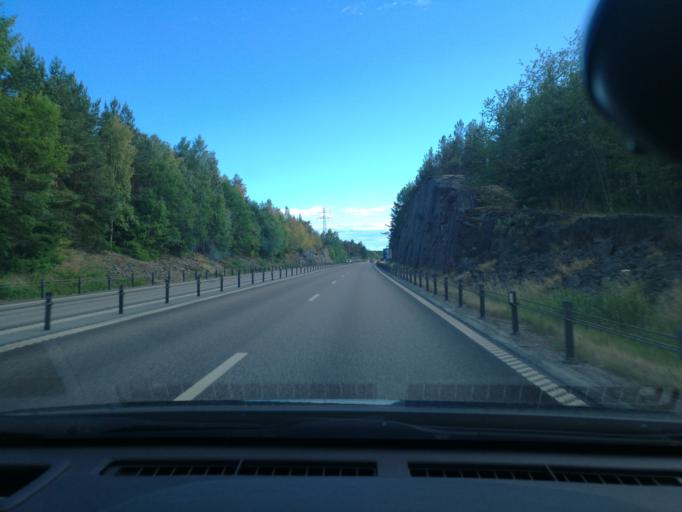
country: SE
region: Kalmar
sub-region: Oskarshamns Kommun
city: Oskarshamn
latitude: 57.2832
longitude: 16.4522
